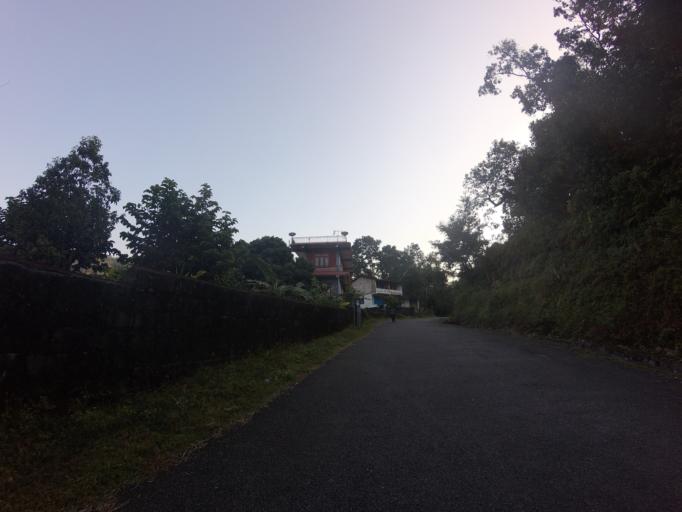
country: NP
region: Western Region
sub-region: Gandaki Zone
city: Pokhara
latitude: 28.2450
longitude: 84.0020
